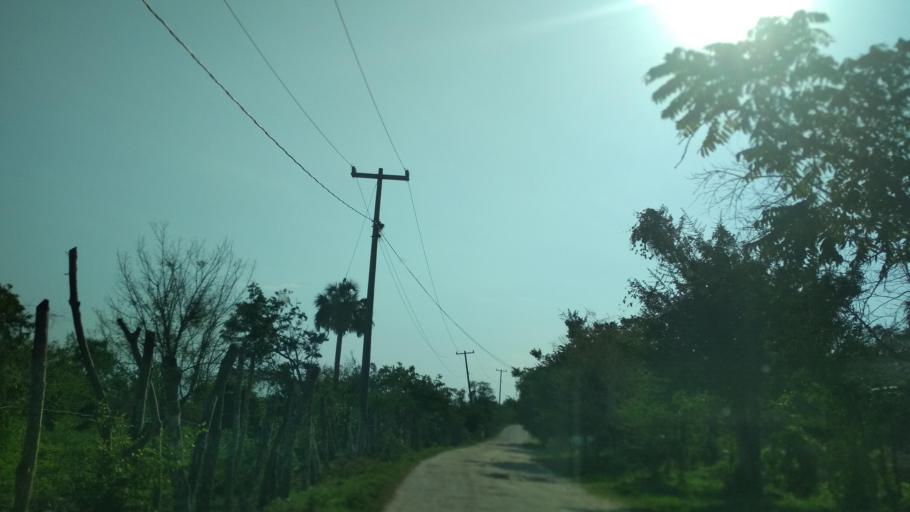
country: MM
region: Shan
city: Taunggyi
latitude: 20.4014
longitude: 97.3292
